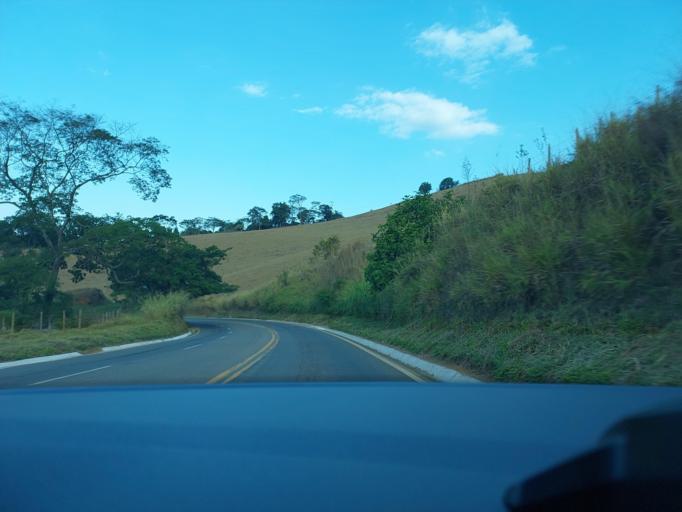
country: BR
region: Minas Gerais
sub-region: Muriae
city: Muriae
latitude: -21.0912
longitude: -42.4817
